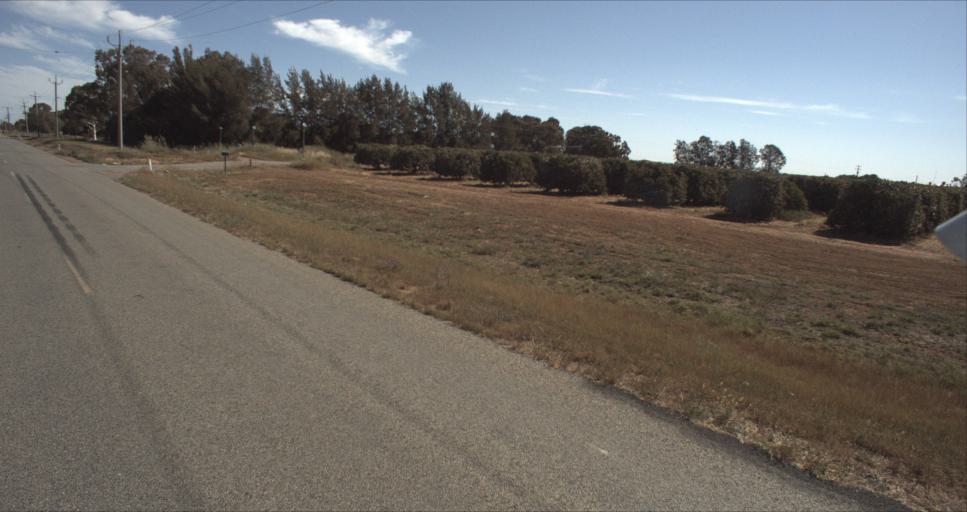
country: AU
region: New South Wales
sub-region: Leeton
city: Leeton
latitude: -34.5612
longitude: 146.3835
